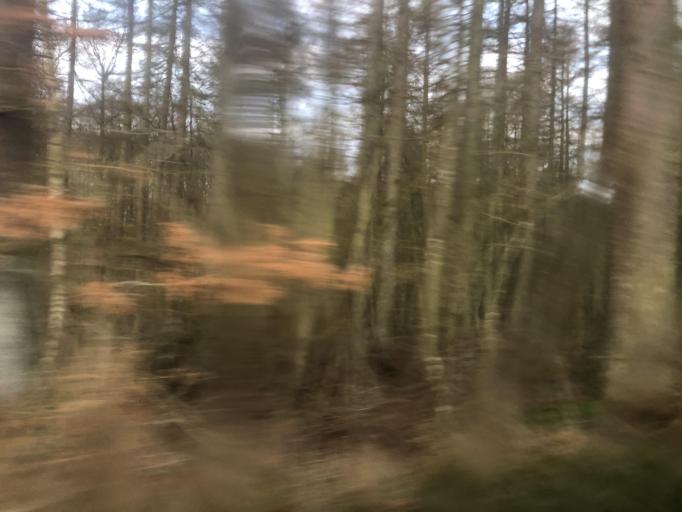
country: SE
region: Skane
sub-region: Lunds Kommun
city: Veberod
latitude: 55.6061
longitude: 13.5373
